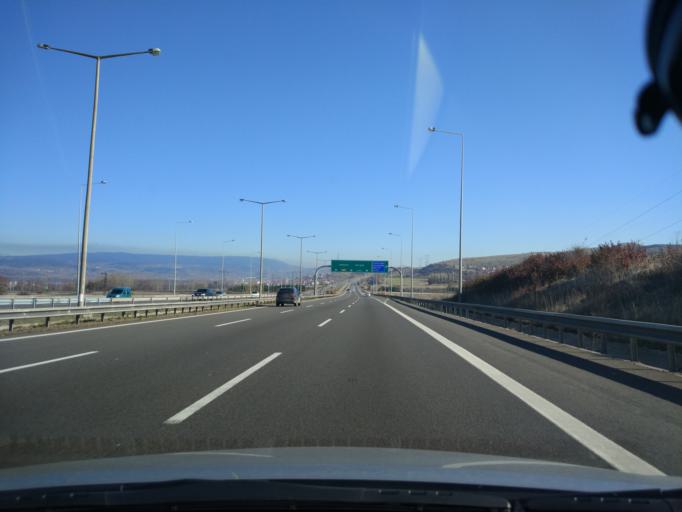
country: TR
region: Bolu
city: Yenicaga
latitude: 40.7626
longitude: 32.0028
